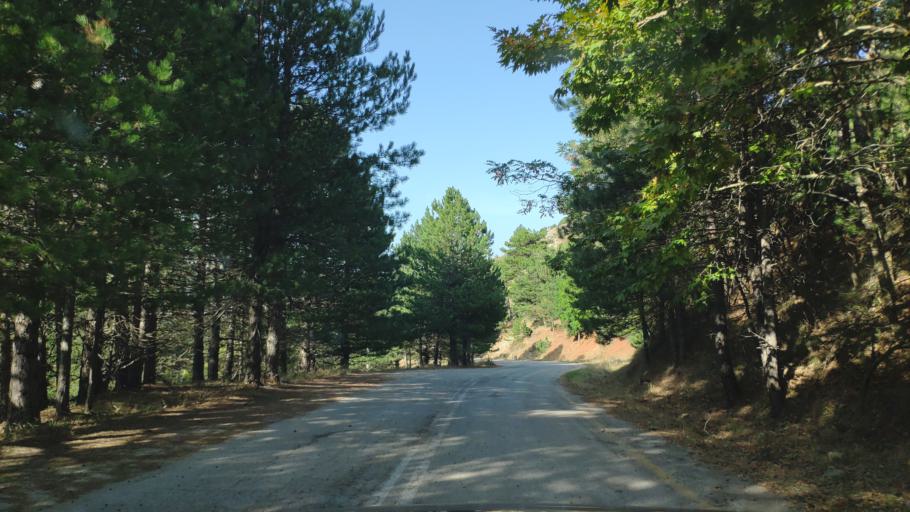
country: GR
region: West Greece
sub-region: Nomos Achaias
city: Aiyira
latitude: 38.0547
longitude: 22.3814
